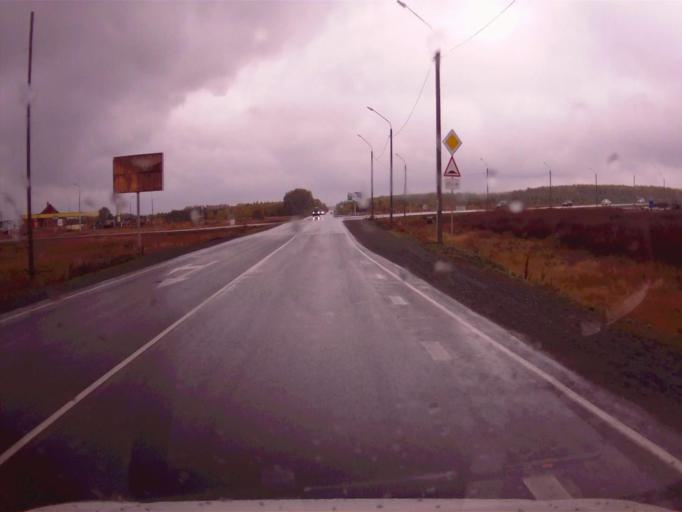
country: RU
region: Chelyabinsk
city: Tayginka
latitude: 55.4997
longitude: 60.6374
